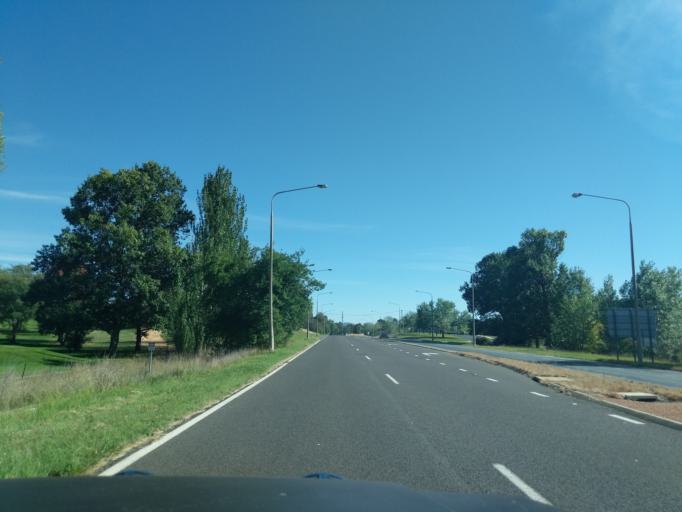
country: AU
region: Australian Capital Territory
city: Forrest
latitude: -35.3415
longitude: 149.1528
